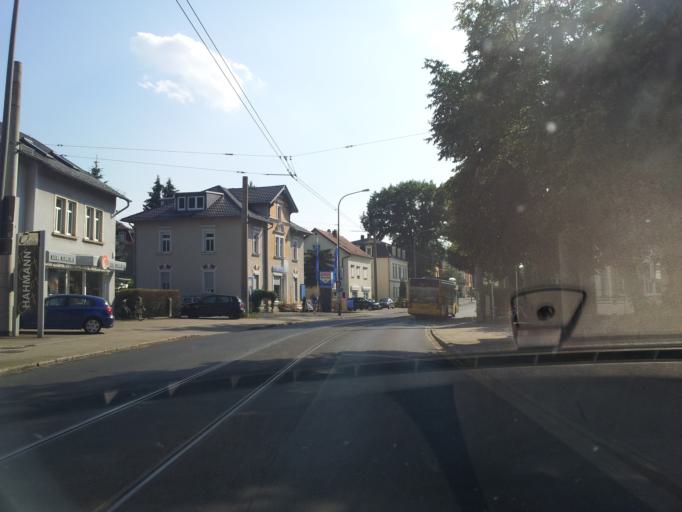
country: DE
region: Saxony
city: Albertstadt
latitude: 51.1157
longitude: 13.7865
